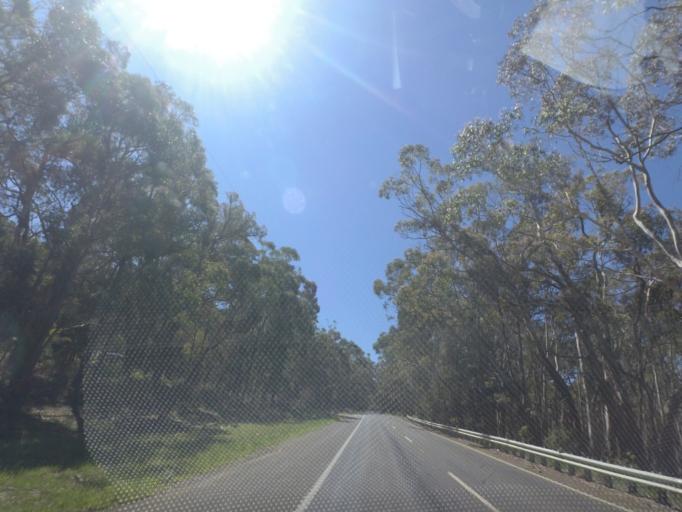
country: AU
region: Victoria
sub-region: Hume
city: Sunbury
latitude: -37.2302
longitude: 144.7407
